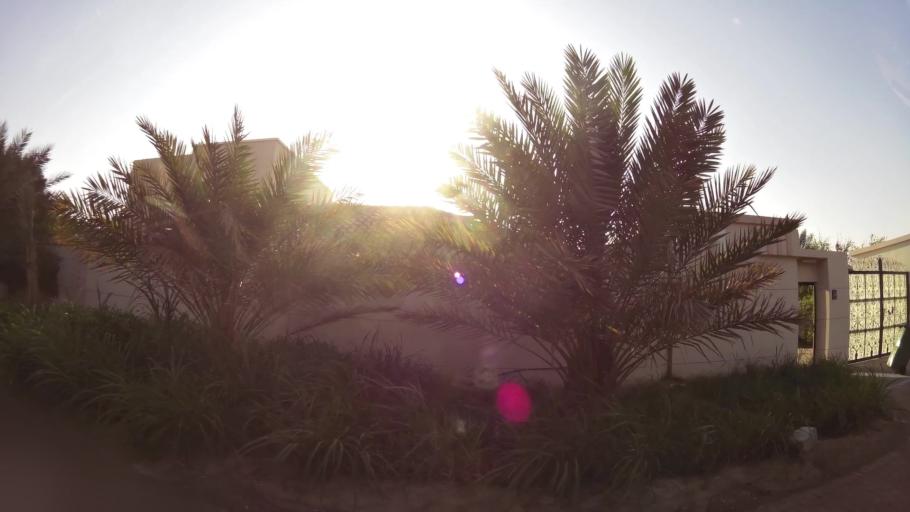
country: AE
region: Abu Dhabi
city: Al Ain
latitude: 24.0787
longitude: 55.8370
